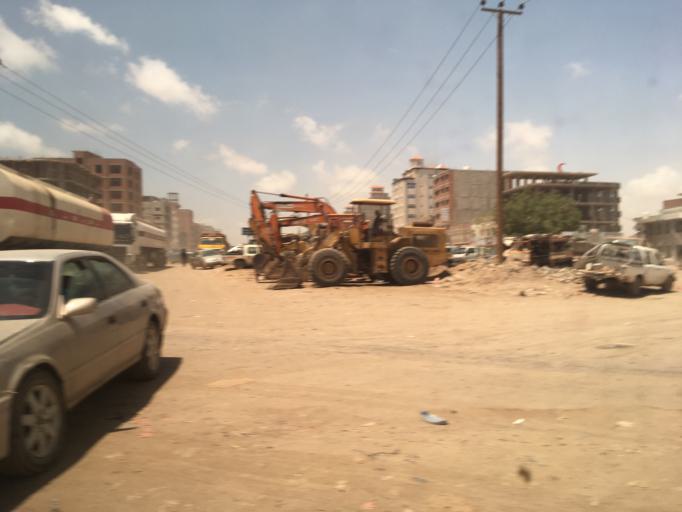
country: YE
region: Aden
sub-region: Al Mansura
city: Al Mansurah
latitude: 12.8681
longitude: 44.9705
